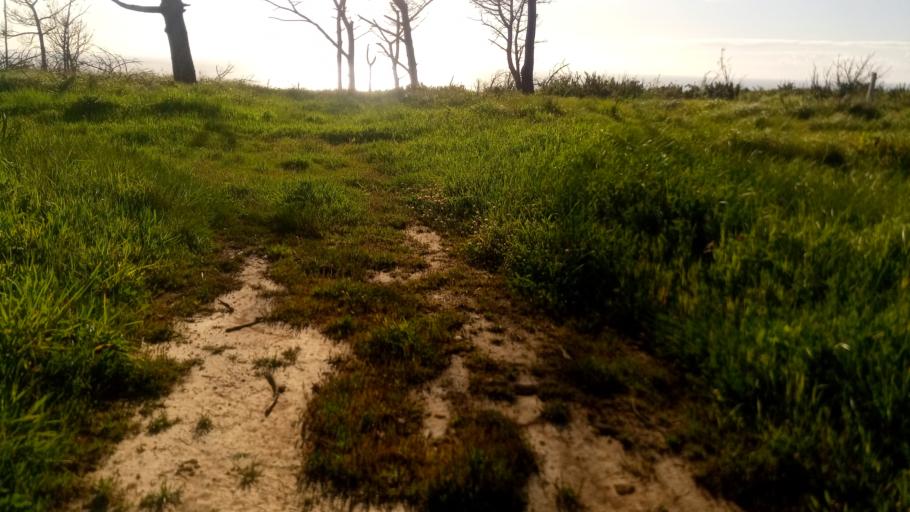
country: PT
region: Leiria
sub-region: Caldas da Rainha
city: Caldas da Rainha
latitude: 39.4627
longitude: -9.1998
